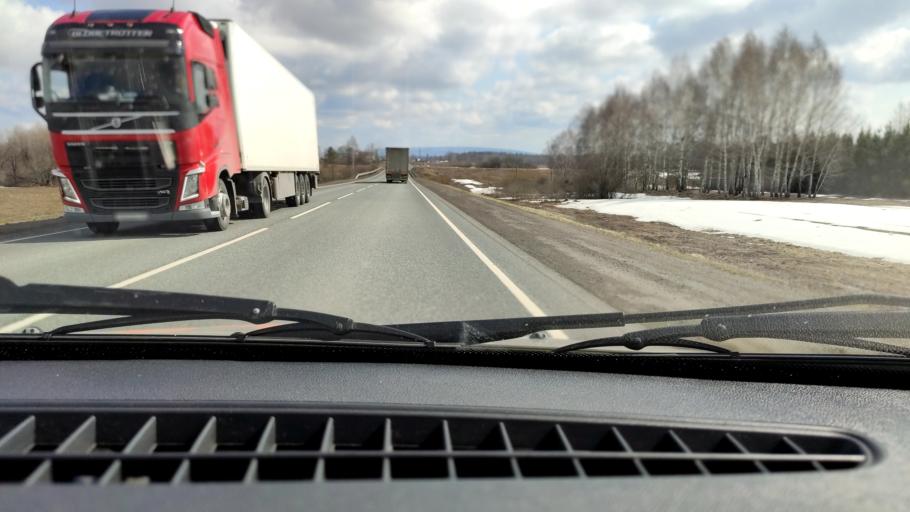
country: RU
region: Bashkortostan
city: Kudeyevskiy
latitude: 54.8167
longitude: 56.7240
